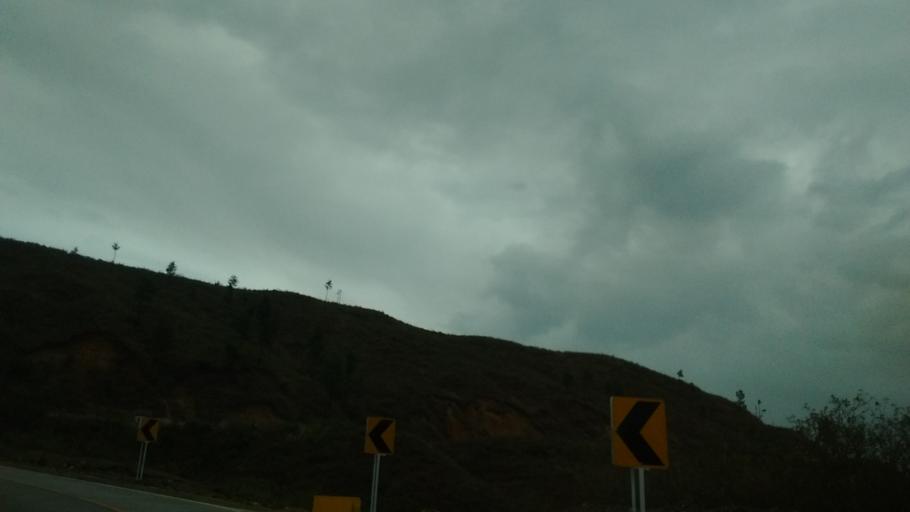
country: CO
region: Cauca
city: La Sierra
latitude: 2.1508
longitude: -76.7774
